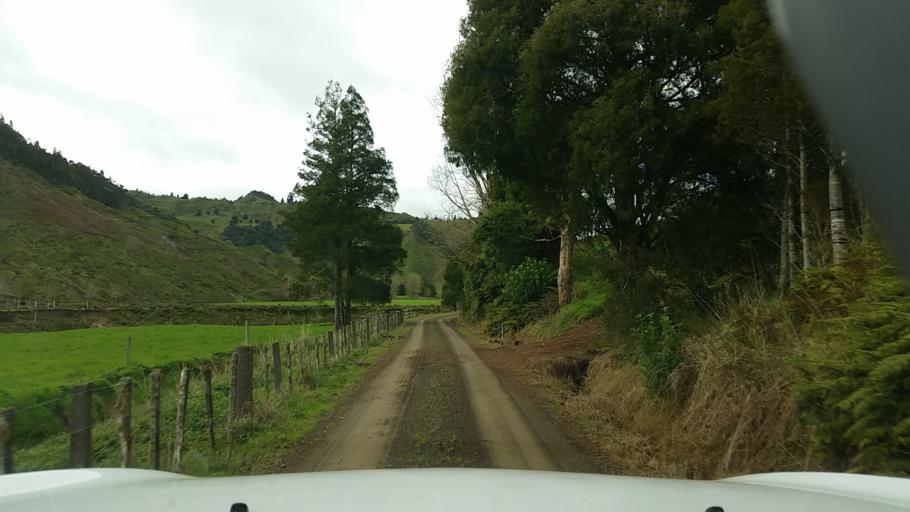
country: NZ
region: Taranaki
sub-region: New Plymouth District
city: Waitara
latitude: -38.7550
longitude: 174.7011
